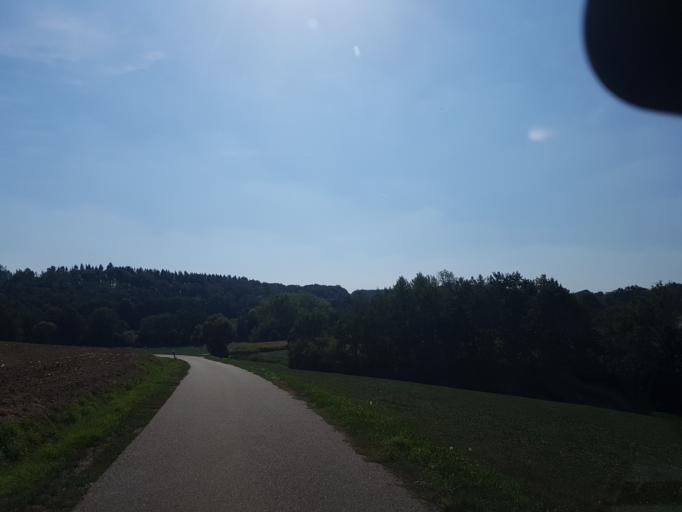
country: DE
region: Saxony
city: Kriebstein
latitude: 51.0508
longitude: 12.9837
